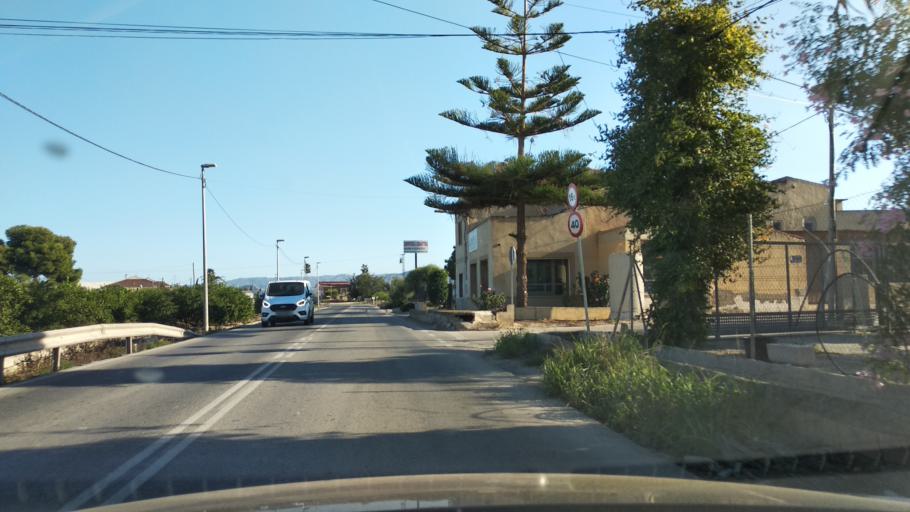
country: ES
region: Murcia
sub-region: Murcia
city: Santomera
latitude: 38.0465
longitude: -1.0540
